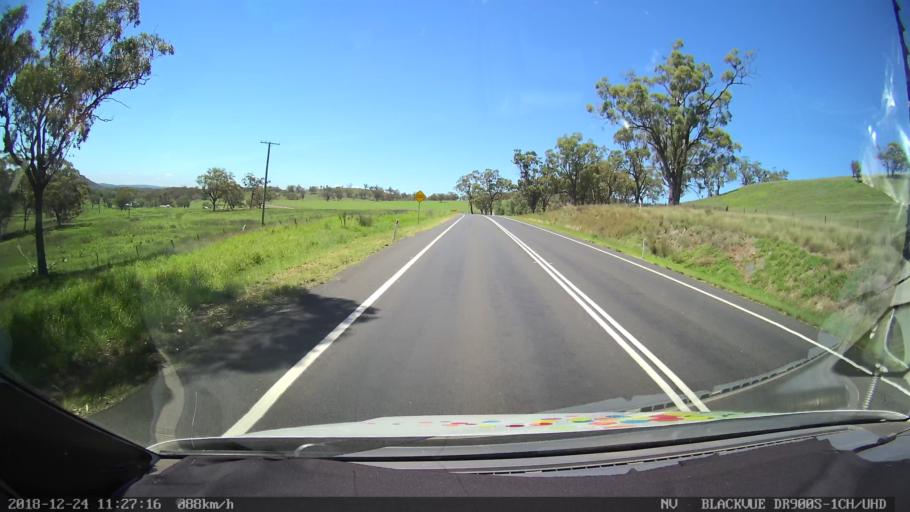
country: AU
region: New South Wales
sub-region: Upper Hunter Shire
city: Merriwa
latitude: -32.1800
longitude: 150.4345
